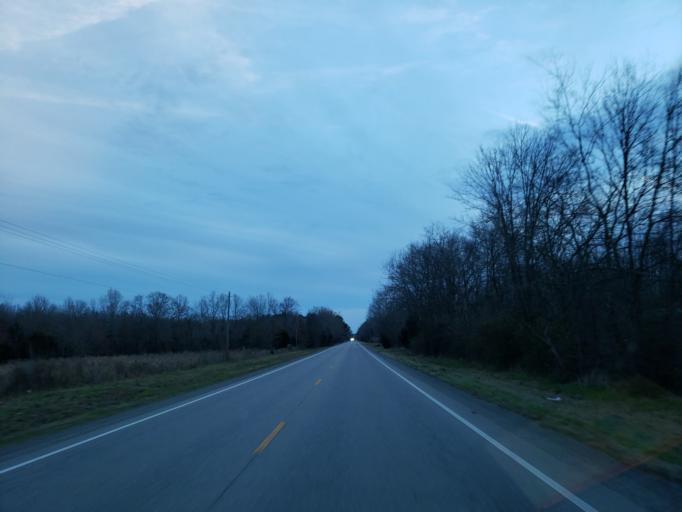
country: US
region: Alabama
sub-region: Sumter County
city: Livingston
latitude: 32.8262
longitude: -88.3099
